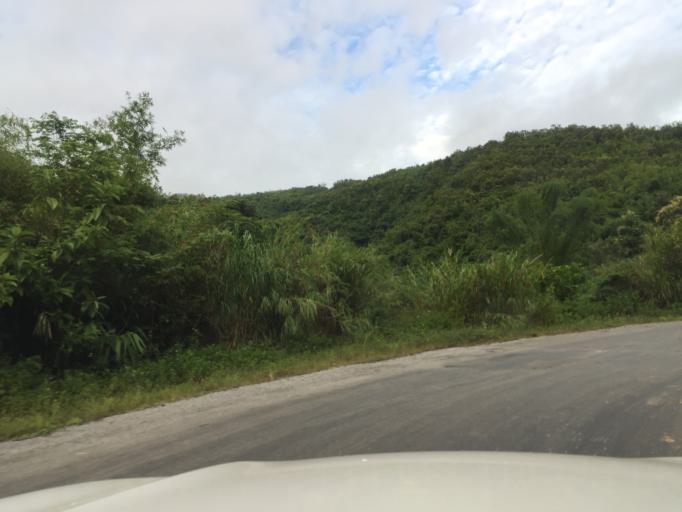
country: LA
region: Phongsali
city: Khoa
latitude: 21.1011
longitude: 102.2754
